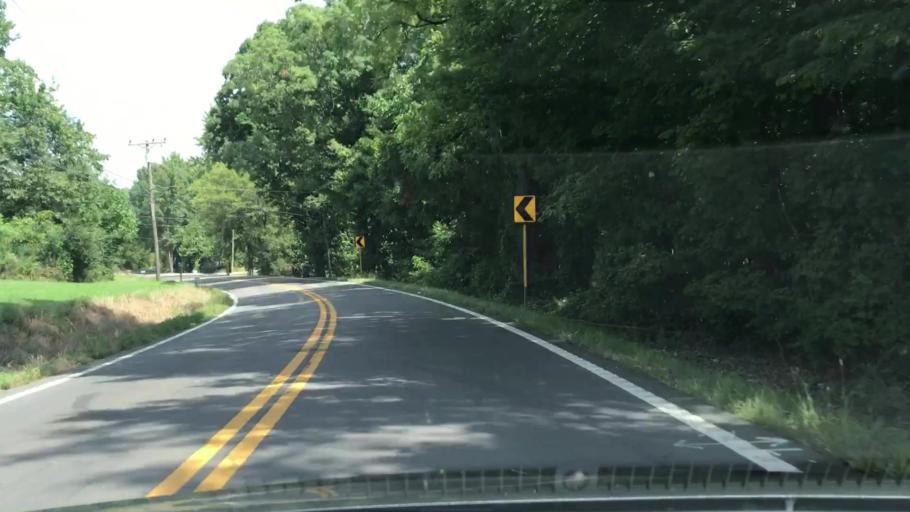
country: US
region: Tennessee
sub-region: Sumner County
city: Portland
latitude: 36.5174
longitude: -86.5626
